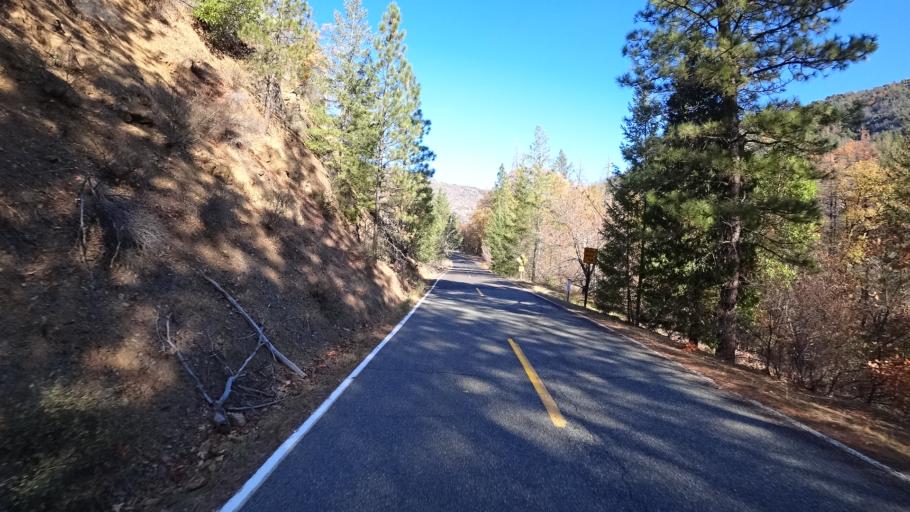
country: US
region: California
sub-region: Siskiyou County
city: Yreka
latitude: 41.9108
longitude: -122.8364
